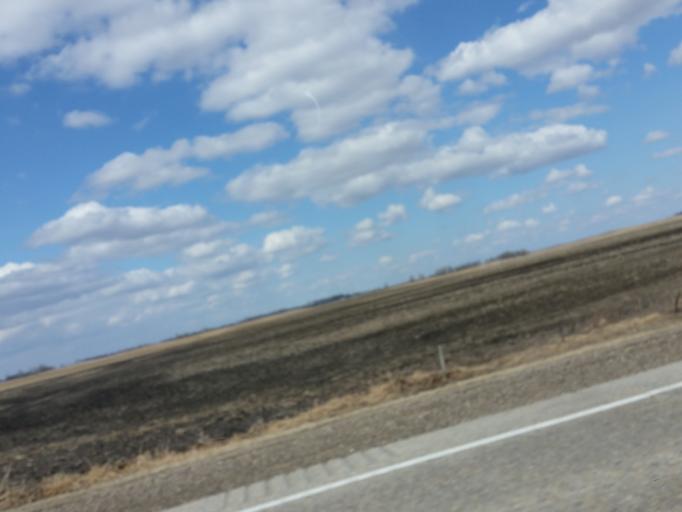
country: US
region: South Dakota
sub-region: Deuel County
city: Clear Lake
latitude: 44.8901
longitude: -96.7867
